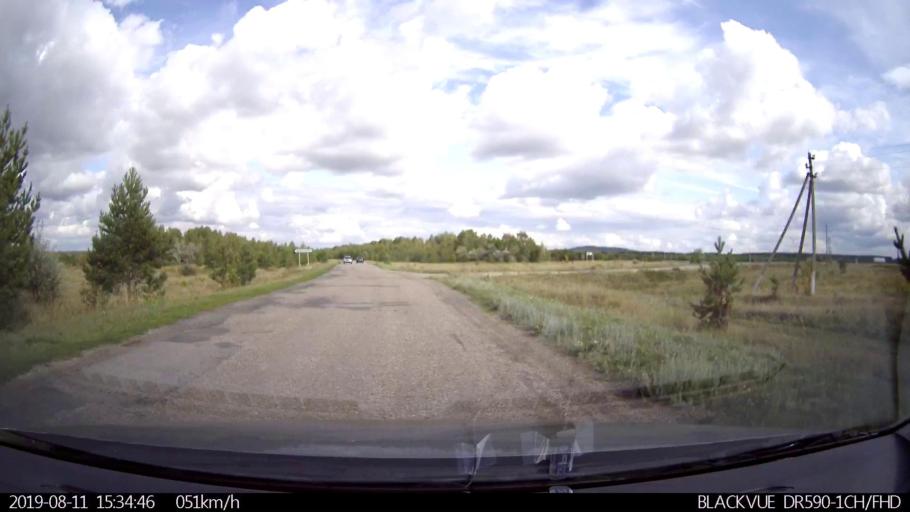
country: RU
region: Ulyanovsk
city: Ignatovka
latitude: 53.8605
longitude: 47.5994
